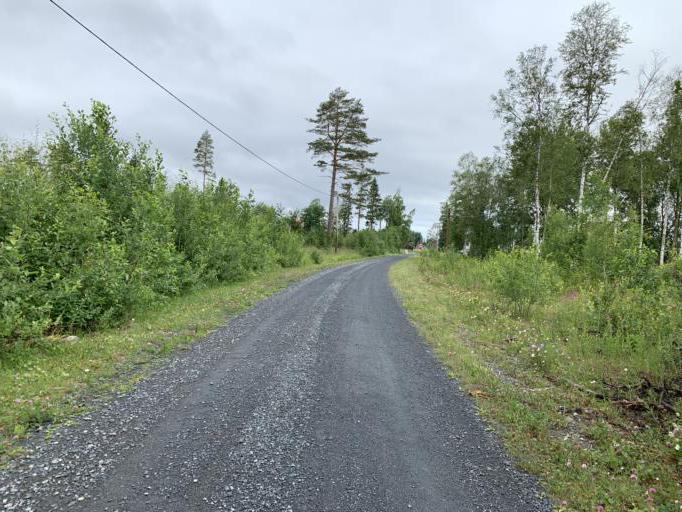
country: SE
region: Jaemtland
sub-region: Krokoms Kommun
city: Valla
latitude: 63.2338
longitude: 14.0222
